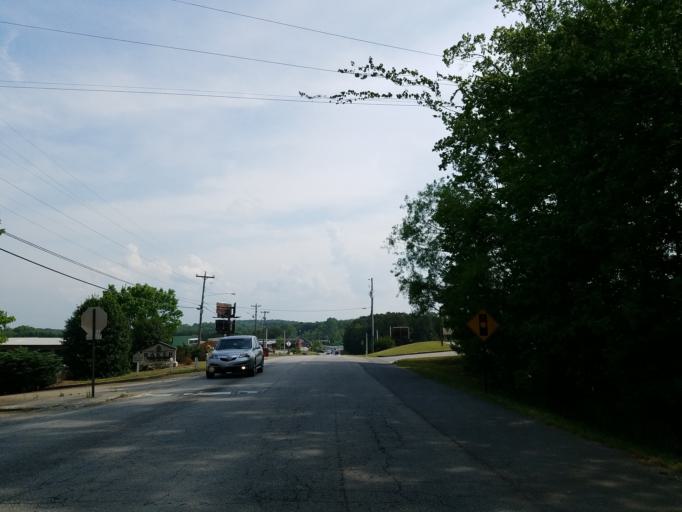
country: US
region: Georgia
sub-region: Paulding County
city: Dallas
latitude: 33.9045
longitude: -84.8021
